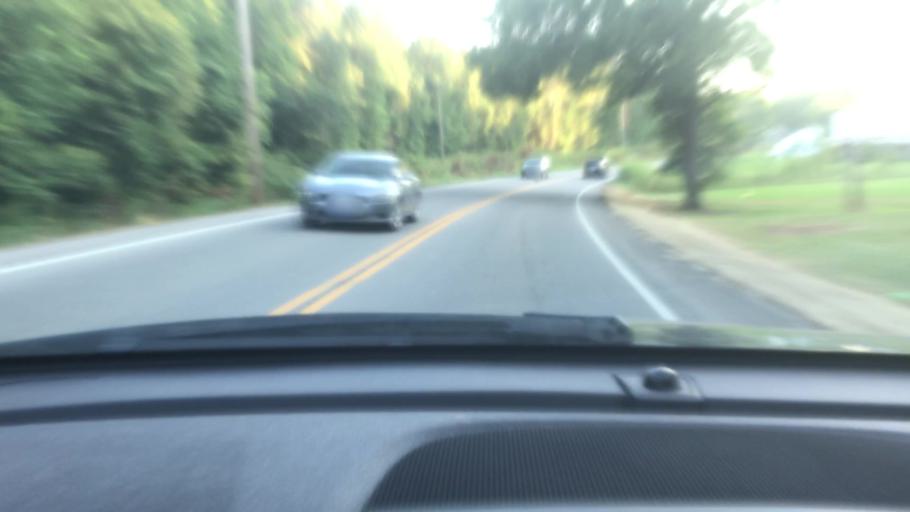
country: US
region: Tennessee
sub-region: Dickson County
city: Dickson
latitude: 36.1204
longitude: -87.3640
